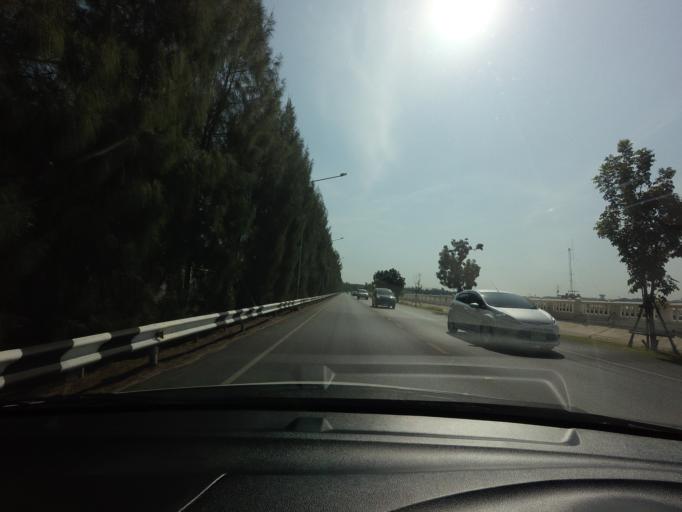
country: TH
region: Bangkok
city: Sai Mai
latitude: 13.9351
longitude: 100.6165
